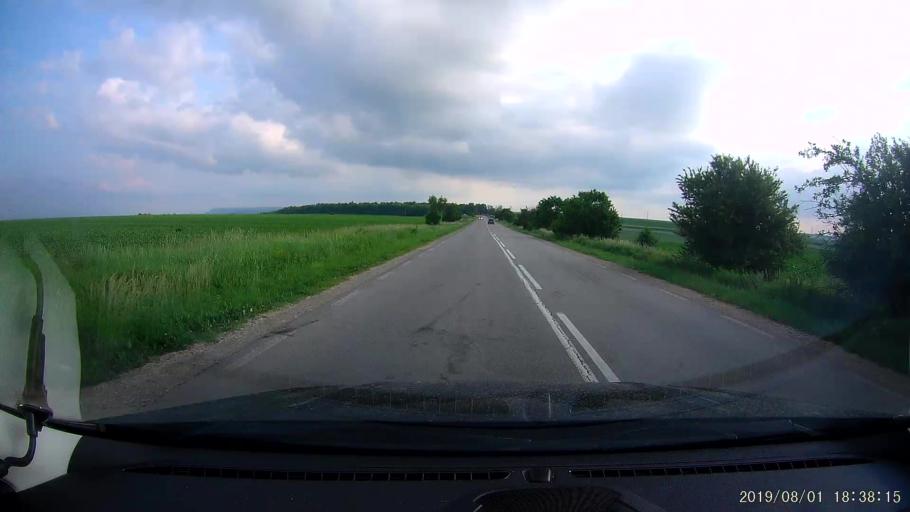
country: BG
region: Shumen
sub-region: Obshtina Khitrino
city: Gara Khitrino
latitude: 43.4050
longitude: 26.9190
